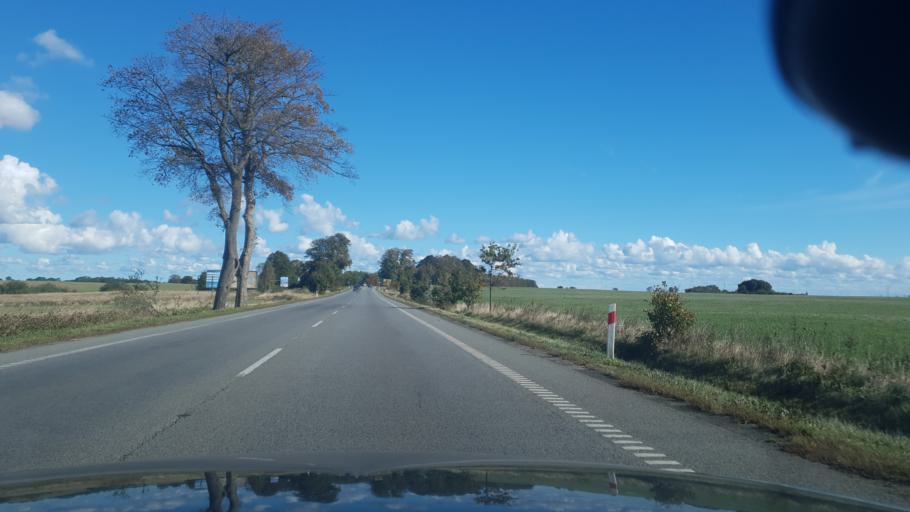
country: PL
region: Pomeranian Voivodeship
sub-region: Powiat wejherowski
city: Rekowo Dolne
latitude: 54.6678
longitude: 18.3692
